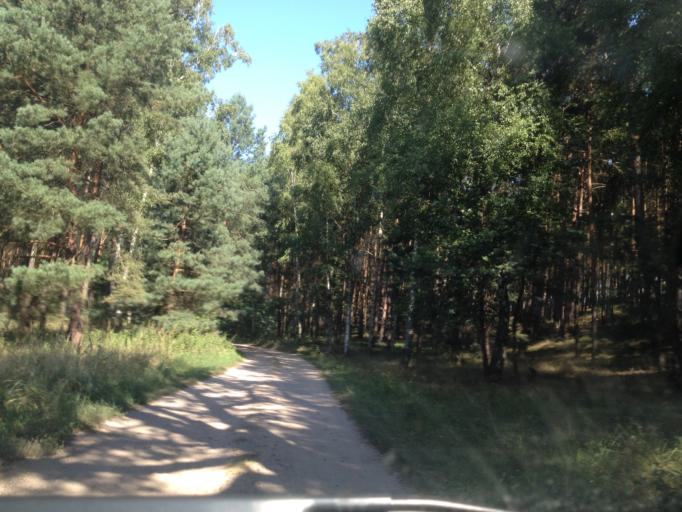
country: PL
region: Greater Poland Voivodeship
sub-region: Powiat sredzki
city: Zaniemysl
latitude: 52.1050
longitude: 17.1305
